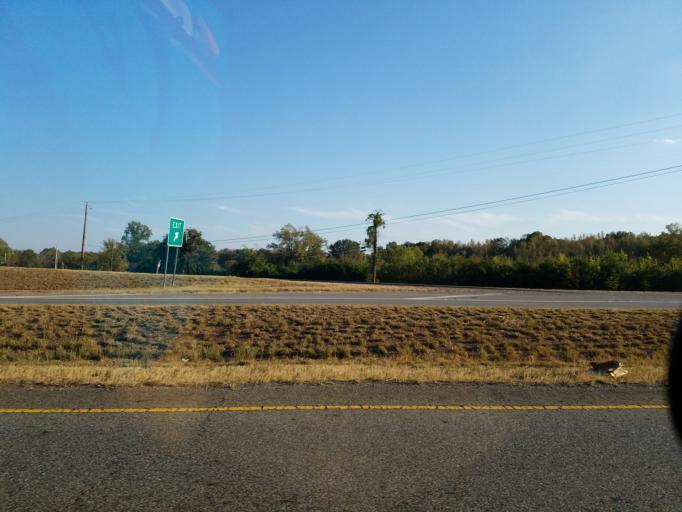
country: US
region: Georgia
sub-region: Bartow County
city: Cartersville
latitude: 34.2206
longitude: -84.8515
